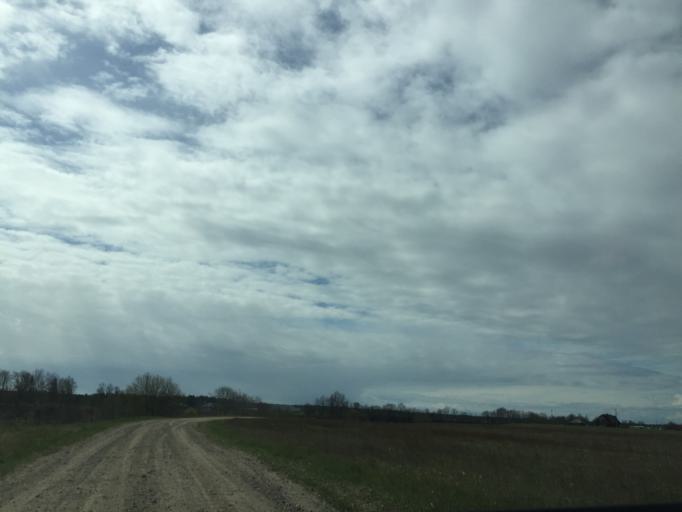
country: LV
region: Salacgrivas
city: Salacgriva
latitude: 57.7506
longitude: 24.4007
